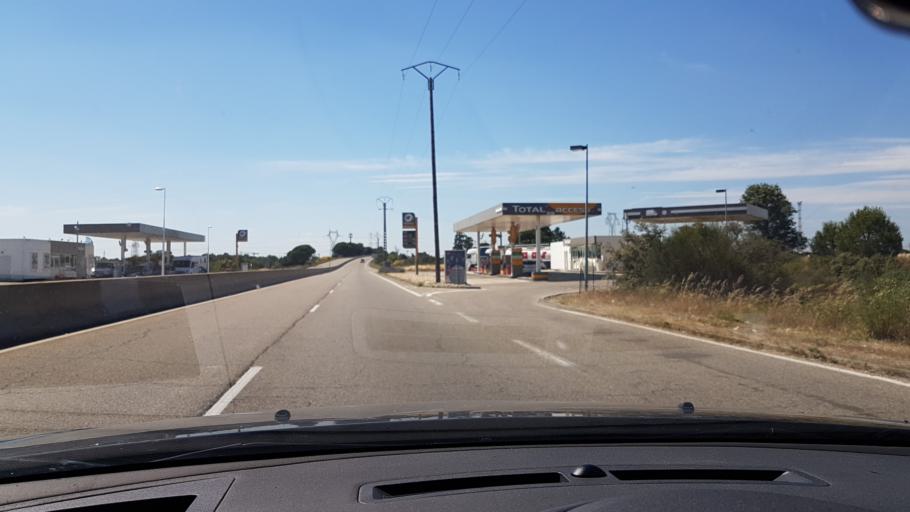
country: FR
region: Provence-Alpes-Cote d'Azur
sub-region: Departement des Bouches-du-Rhone
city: Fos-sur-Mer
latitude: 43.4708
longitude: 4.9090
